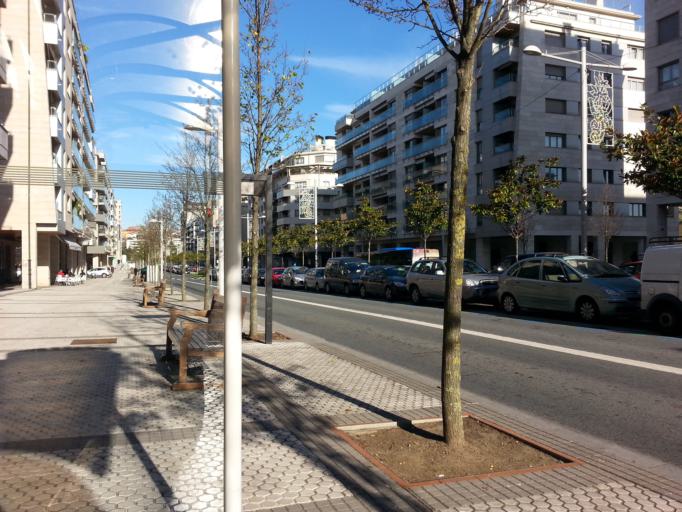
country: ES
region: Basque Country
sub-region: Provincia de Guipuzcoa
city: San Sebastian
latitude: 43.3090
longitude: -1.9713
